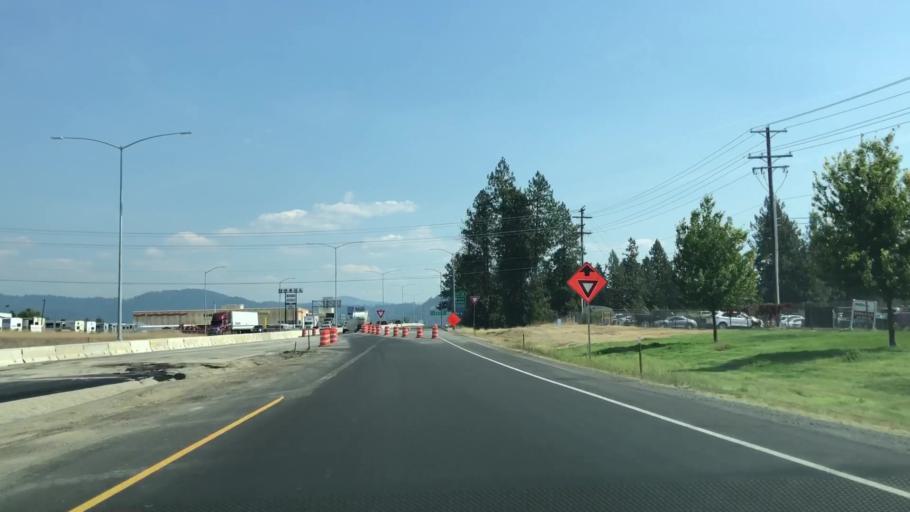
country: US
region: Idaho
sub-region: Kootenai County
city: Coeur d'Alene
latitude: 47.6991
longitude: -116.8039
